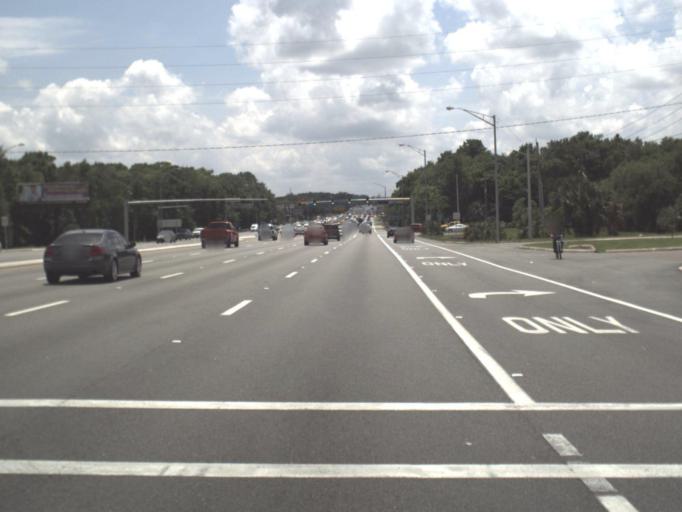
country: US
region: Florida
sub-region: Clay County
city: Bellair-Meadowbrook Terrace
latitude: 30.1938
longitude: -81.7396
